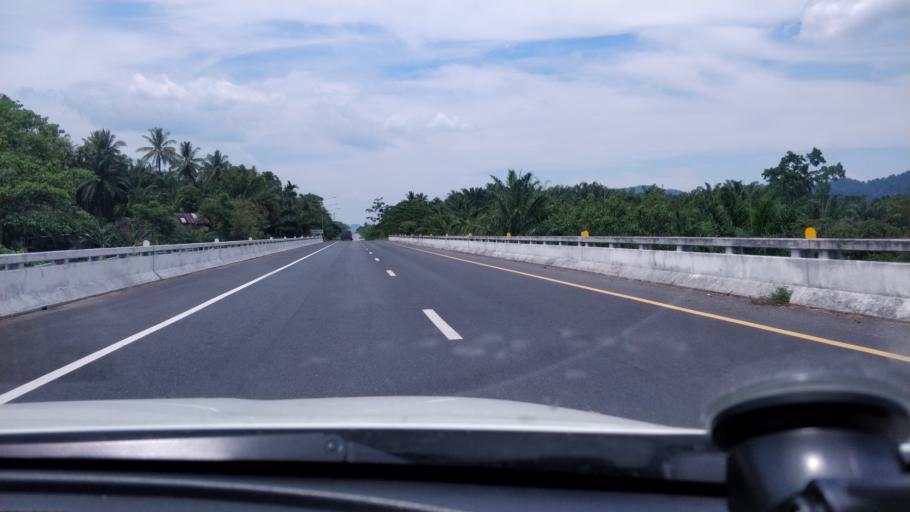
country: TH
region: Krabi
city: Plai Phraya
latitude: 8.5004
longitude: 98.8833
